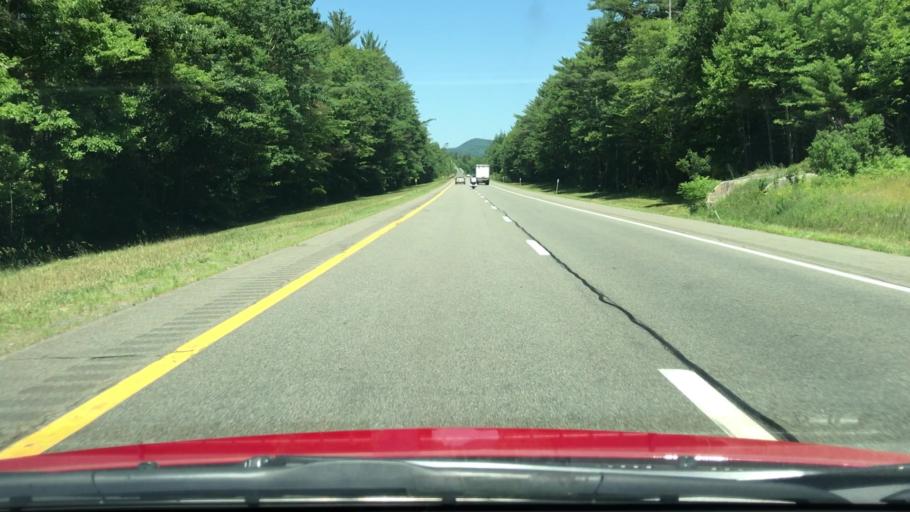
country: US
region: New York
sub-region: Essex County
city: Elizabethtown
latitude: 44.3285
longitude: -73.5305
